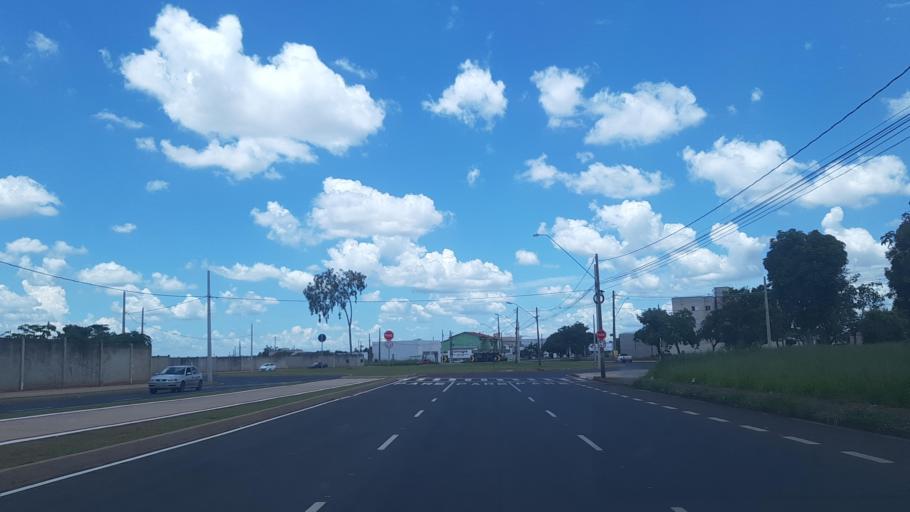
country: BR
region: Minas Gerais
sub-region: Uberlandia
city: Uberlandia
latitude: -18.9519
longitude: -48.3259
